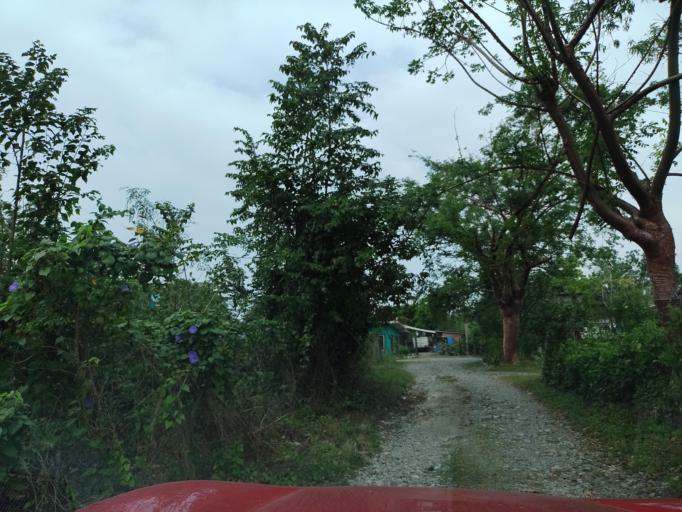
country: MX
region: Veracruz
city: Agua Dulce
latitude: 20.3412
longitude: -97.2947
